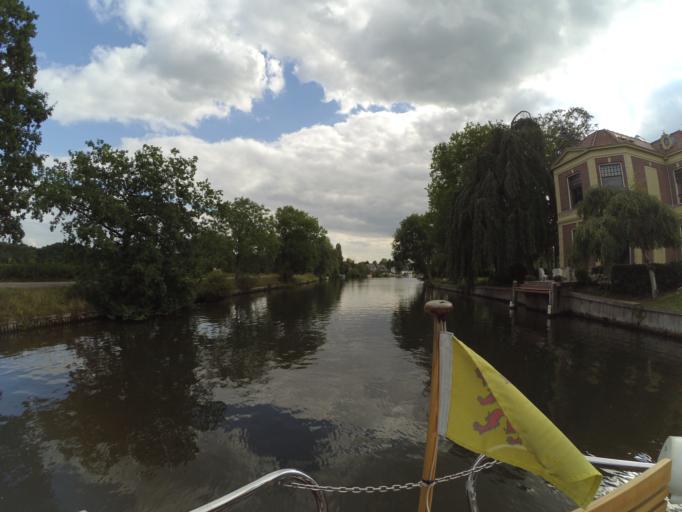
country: NL
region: Utrecht
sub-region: Stichtse Vecht
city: Spechtenkamp
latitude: 52.1573
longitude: 5.0200
